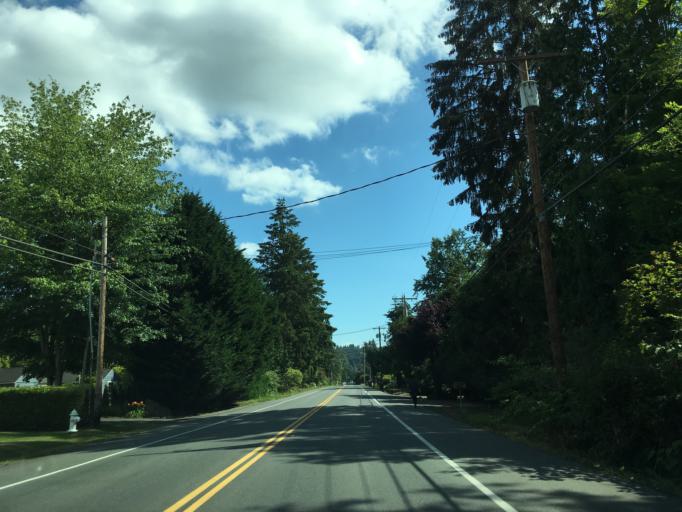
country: US
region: Washington
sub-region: King County
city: Kenmore
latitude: 47.7649
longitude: -122.2335
